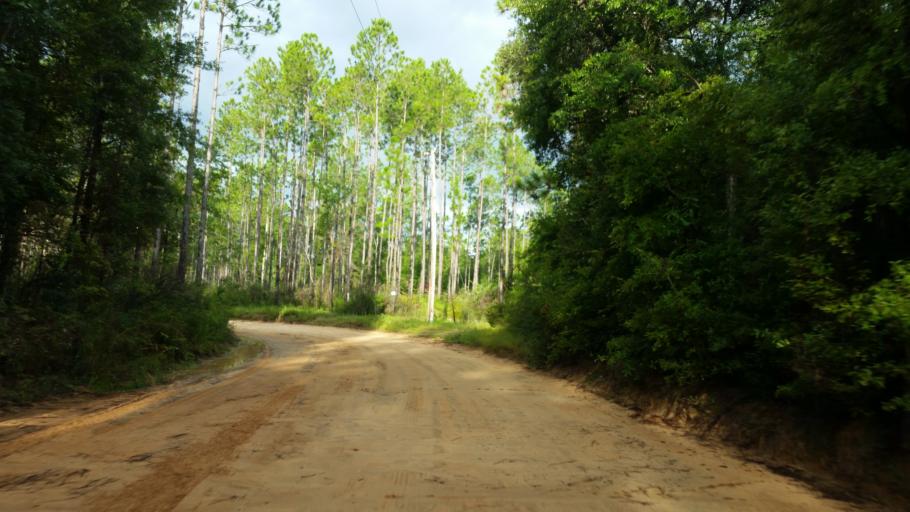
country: US
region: Florida
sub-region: Okaloosa County
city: Crestview
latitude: 30.6694
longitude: -86.7594
